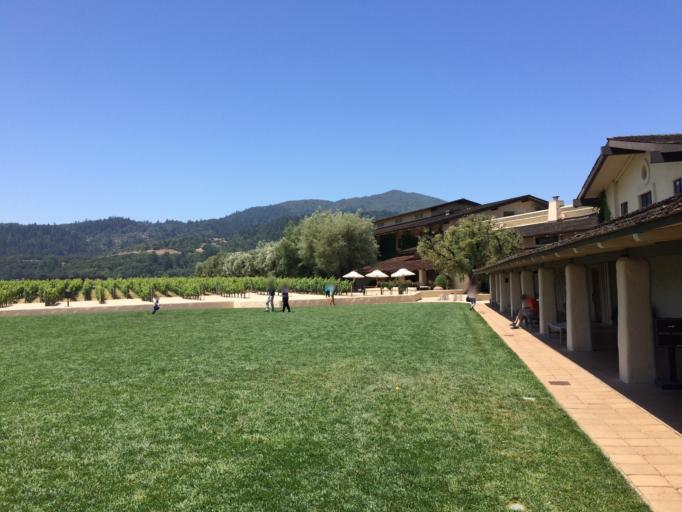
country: US
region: California
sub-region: Napa County
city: Yountville
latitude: 38.4411
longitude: -122.4094
